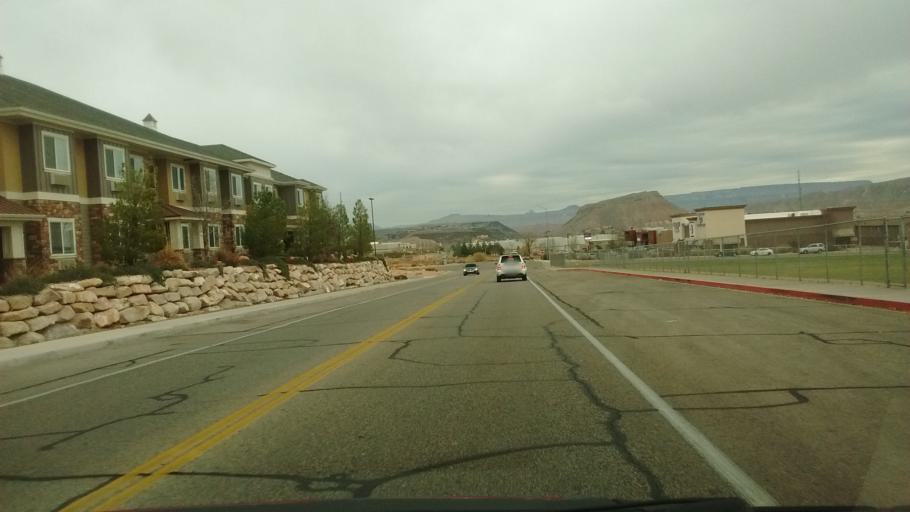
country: US
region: Utah
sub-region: Washington County
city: Washington
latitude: 37.1229
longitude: -113.5298
